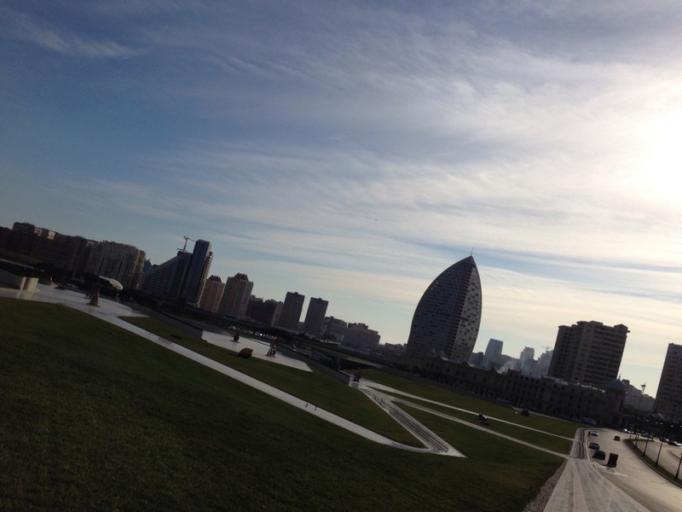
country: AZ
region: Baki
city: Baku
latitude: 40.3954
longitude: 49.8652
